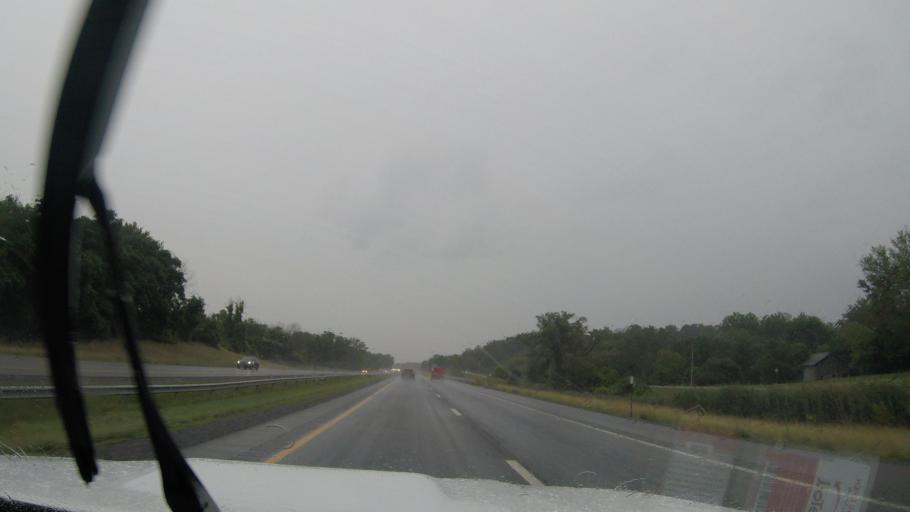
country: US
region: New York
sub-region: Cayuga County
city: Port Byron
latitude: 43.0036
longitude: -76.7103
